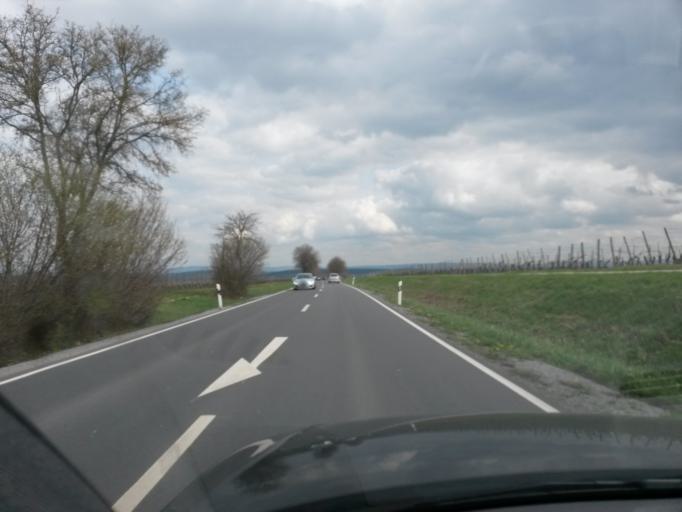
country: DE
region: Bavaria
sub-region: Regierungsbezirk Unterfranken
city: Nordheim
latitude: 49.8677
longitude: 10.1875
